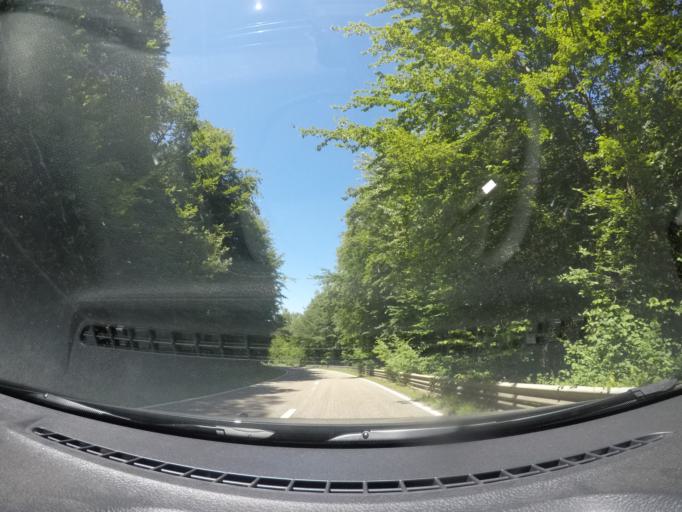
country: BE
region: Wallonia
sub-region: Province du Luxembourg
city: Daverdisse
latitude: 50.0330
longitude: 5.1637
